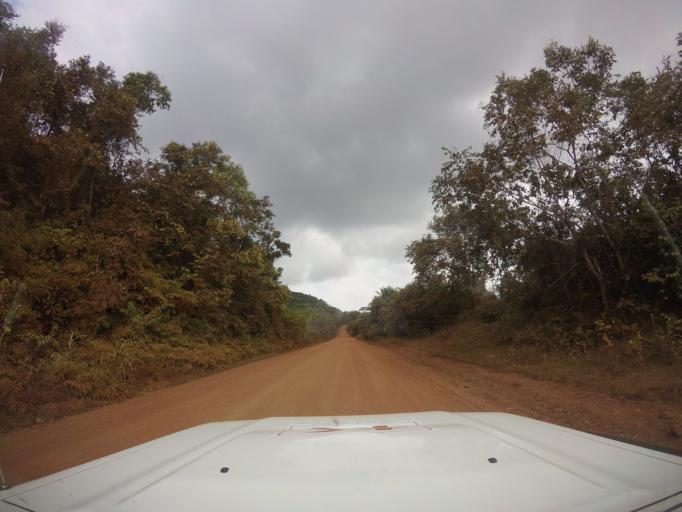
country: LR
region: Grand Cape Mount
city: Robertsport
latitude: 6.7141
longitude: -11.3360
